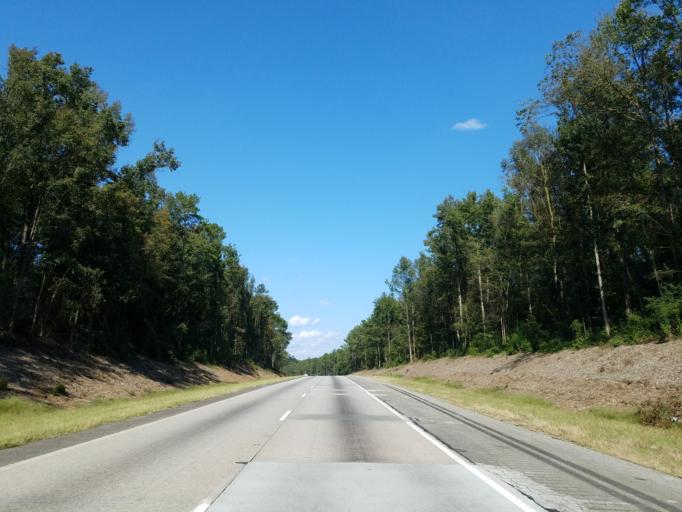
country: US
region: Georgia
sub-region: Jackson County
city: Commerce
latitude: 34.2684
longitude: -83.4420
